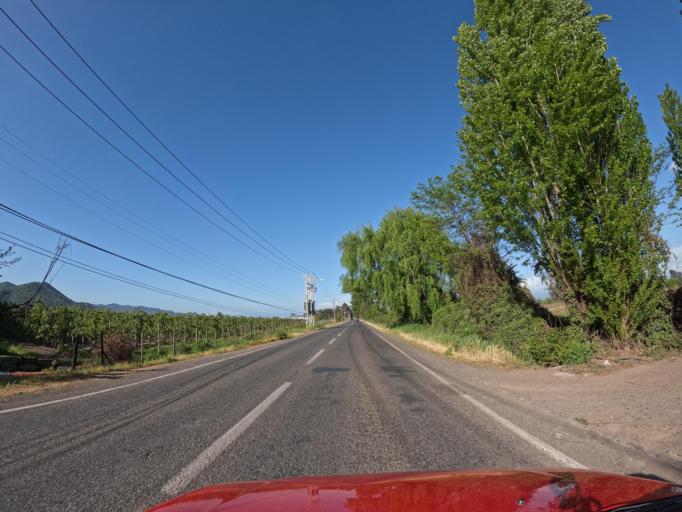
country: CL
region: Maule
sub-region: Provincia de Curico
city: Teno
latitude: -34.8688
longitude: -71.2148
